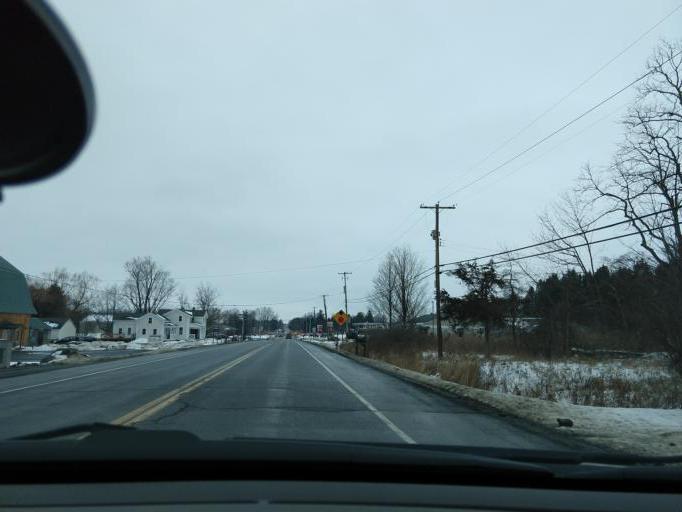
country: US
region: New York
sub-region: Tompkins County
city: Lansing
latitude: 42.5366
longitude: -76.4925
